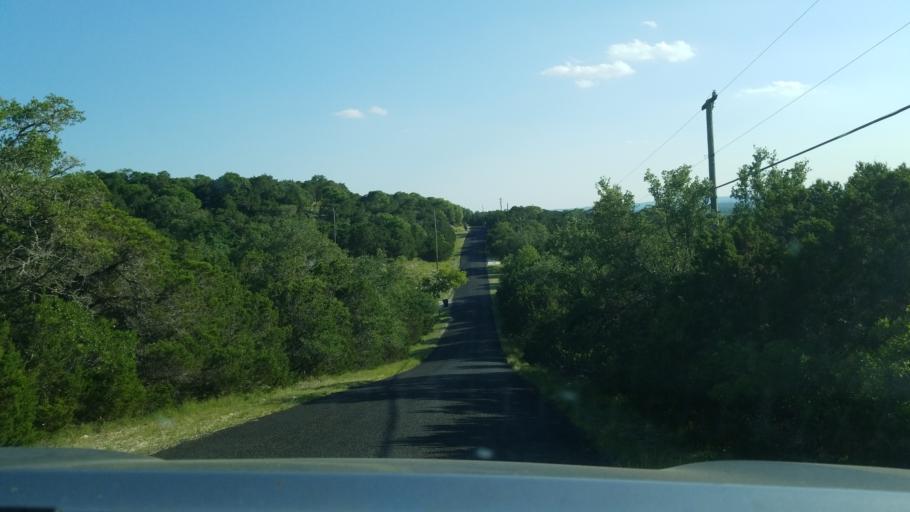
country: US
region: Texas
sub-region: Comal County
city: Bulverde
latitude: 29.7807
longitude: -98.4543
